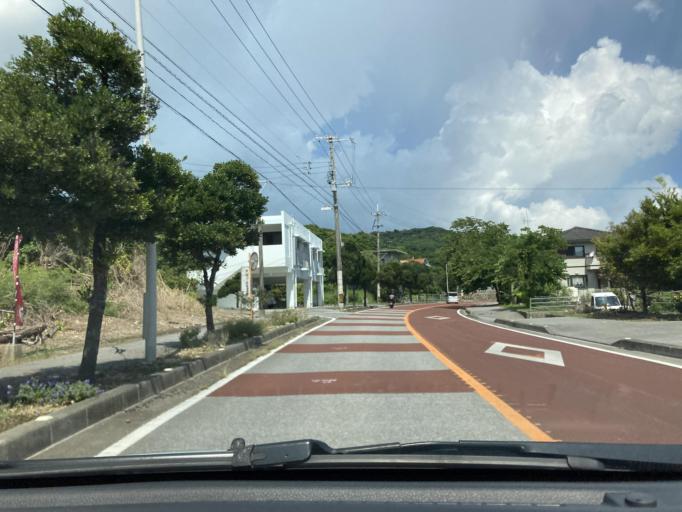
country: JP
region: Okinawa
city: Tomigusuku
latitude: 26.1755
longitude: 127.7676
